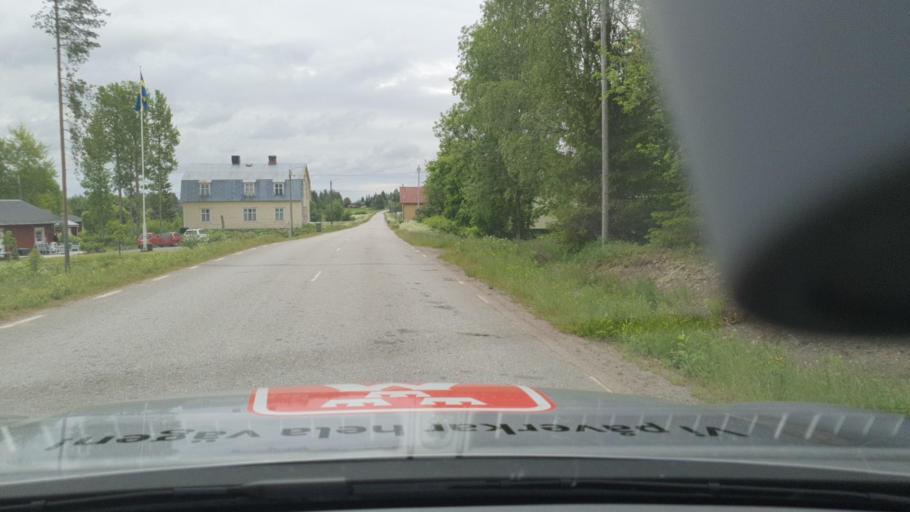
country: SE
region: Norrbotten
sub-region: Lulea Kommun
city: Ranea
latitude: 65.9088
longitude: 22.1752
